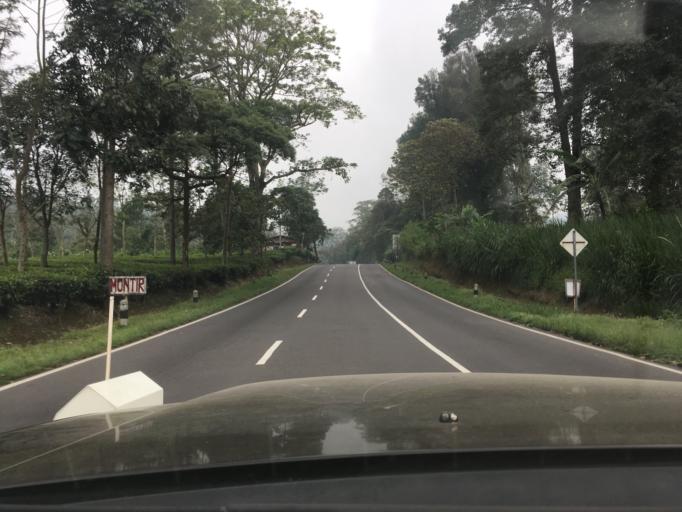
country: ID
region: West Java
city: Lembang
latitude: -6.7662
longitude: 107.6419
